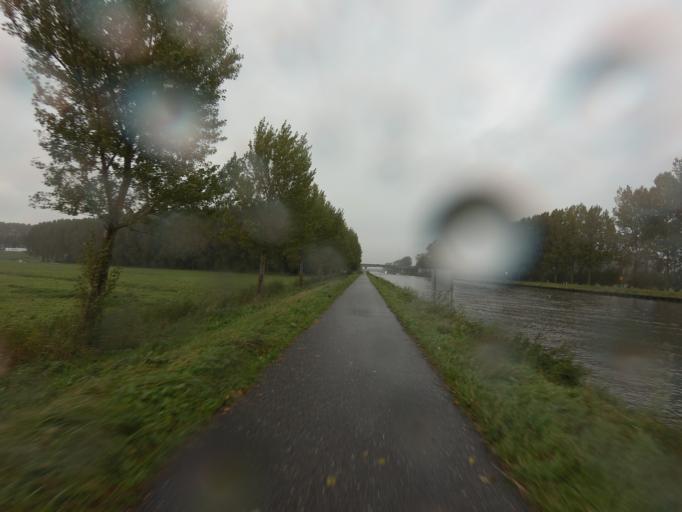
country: NL
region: Utrecht
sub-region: Gemeente Vianen
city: Vianen
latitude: 51.9528
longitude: 5.0527
